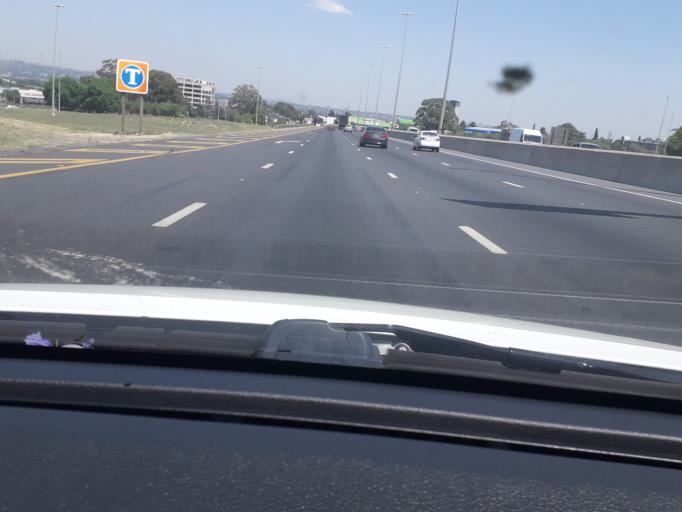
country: ZA
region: Gauteng
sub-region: Ekurhuleni Metropolitan Municipality
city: Germiston
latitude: -26.1635
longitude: 28.1709
